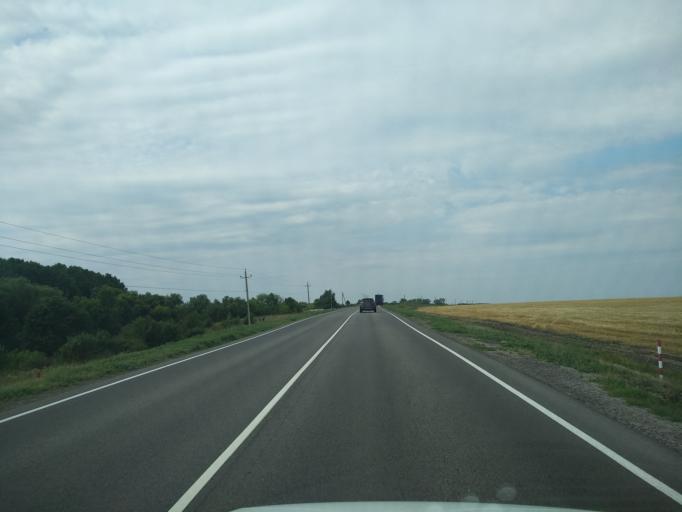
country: RU
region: Voronezj
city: Pereleshinskiy
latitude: 51.8169
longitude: 40.2614
